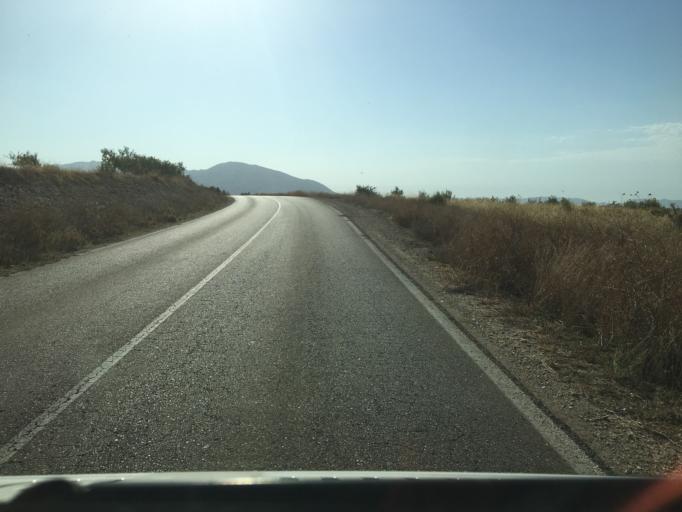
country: ES
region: Andalusia
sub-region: Provincia de Almeria
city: Huercal-Overa
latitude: 37.4700
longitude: -1.9080
